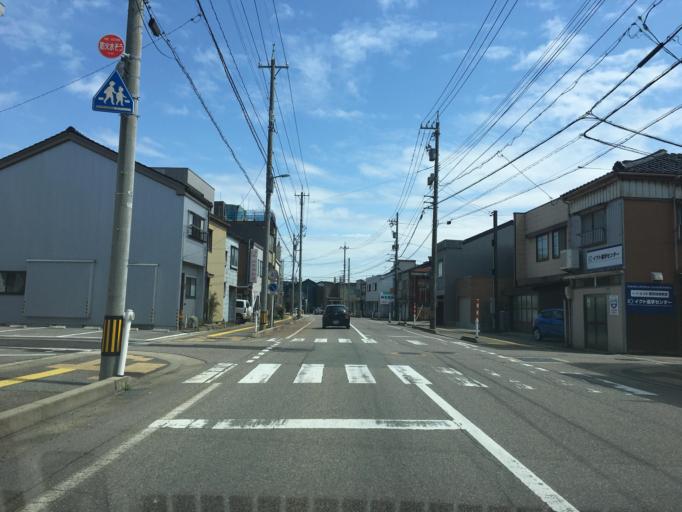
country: JP
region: Toyama
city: Nishishinminato
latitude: 36.7787
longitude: 137.0887
